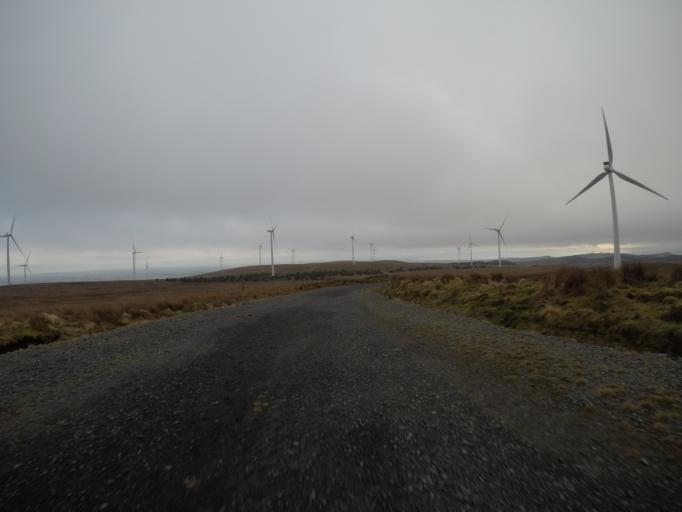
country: GB
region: Scotland
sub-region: North Ayrshire
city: Fairlie
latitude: 55.7423
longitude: -4.7904
